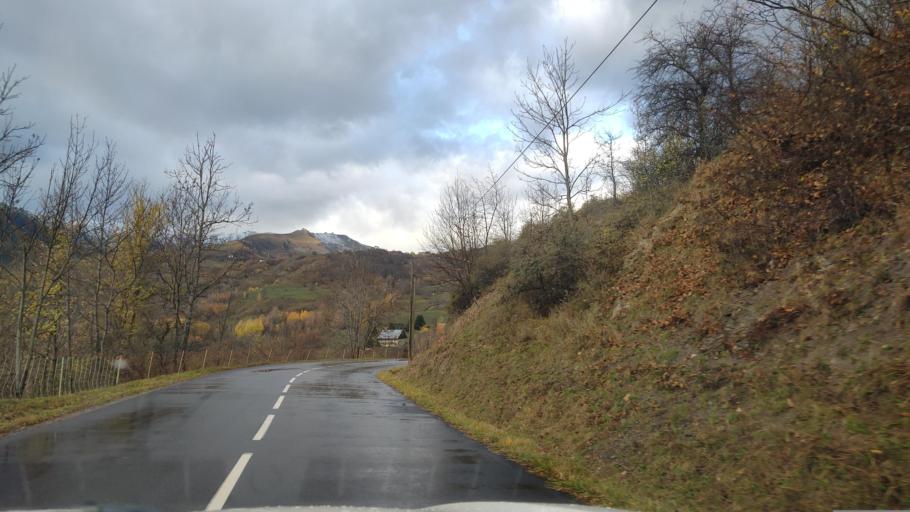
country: FR
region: Rhone-Alpes
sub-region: Departement de la Savoie
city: Saint-Jean-de-Maurienne
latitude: 45.2539
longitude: 6.2964
